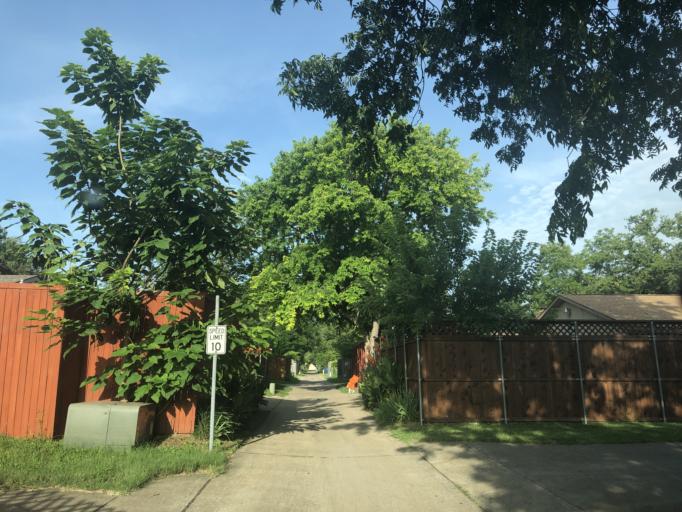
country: US
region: Texas
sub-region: Dallas County
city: Sunnyvale
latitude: 32.8392
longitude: -96.5838
